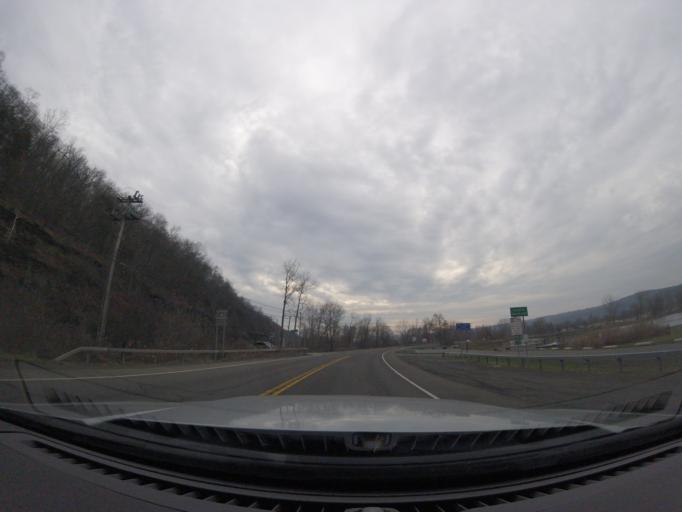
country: US
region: New York
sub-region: Schuyler County
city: Watkins Glen
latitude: 42.3883
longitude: -76.8549
